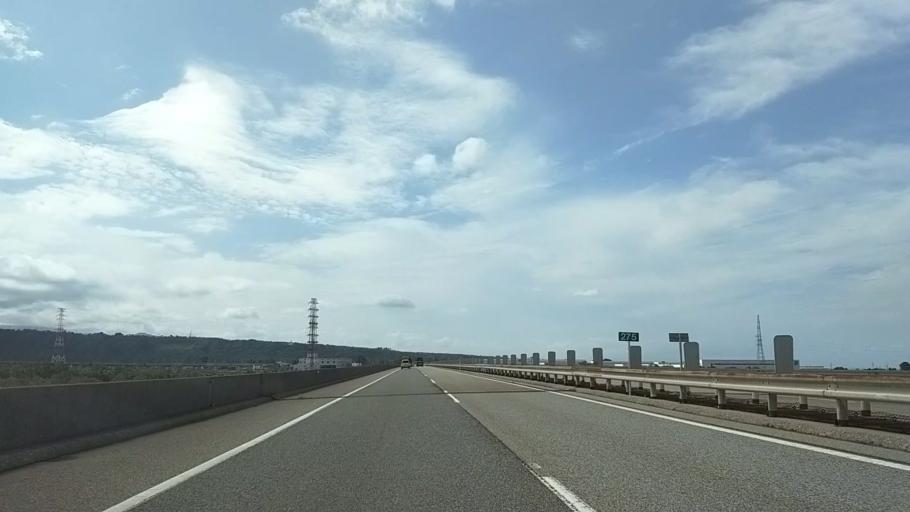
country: JP
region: Toyama
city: Nyuzen
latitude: 36.8956
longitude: 137.4956
